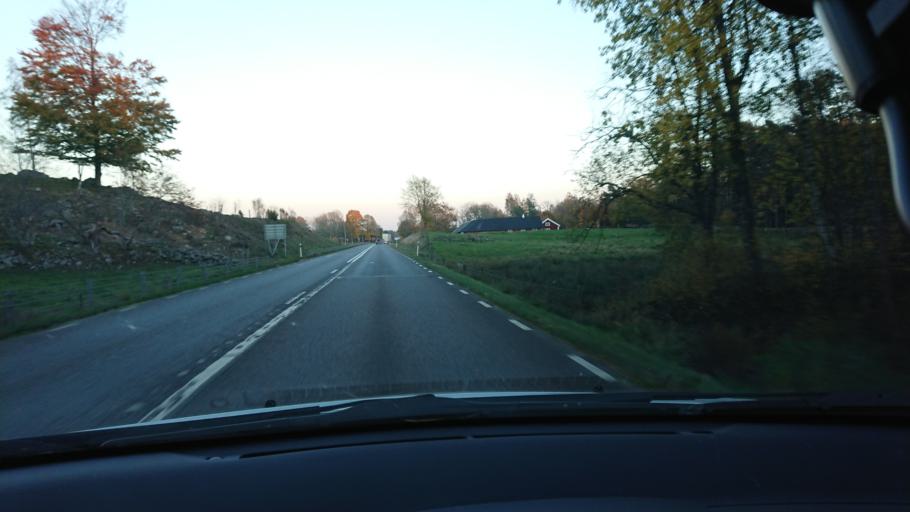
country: SE
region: Halland
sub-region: Laholms Kommun
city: Knared
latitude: 56.7144
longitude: 13.2400
